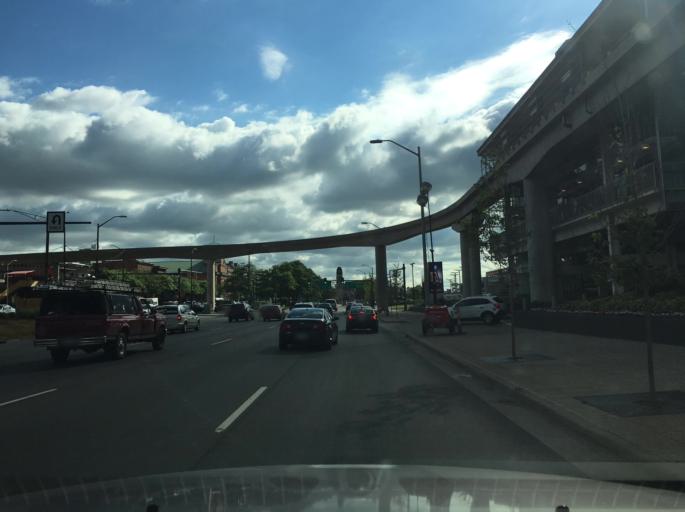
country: US
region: Michigan
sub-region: Wayne County
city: Detroit
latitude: 42.3301
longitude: -83.0406
